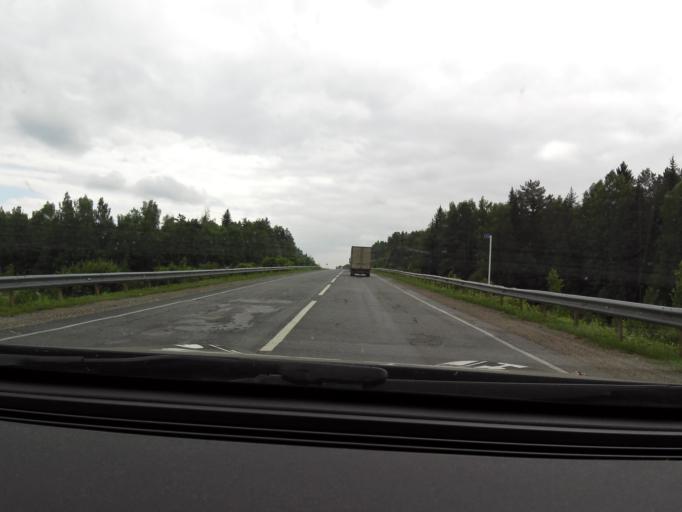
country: RU
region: Perm
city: Suksun
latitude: 57.1382
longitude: 57.2969
